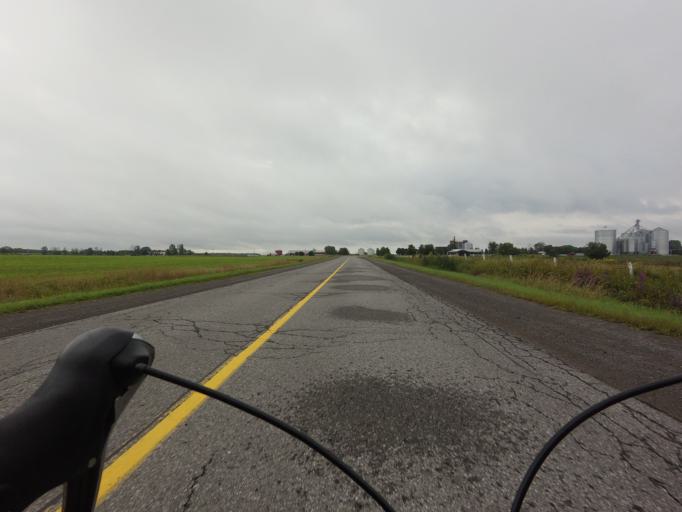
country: CA
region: Ontario
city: Bells Corners
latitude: 45.1423
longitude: -75.7761
